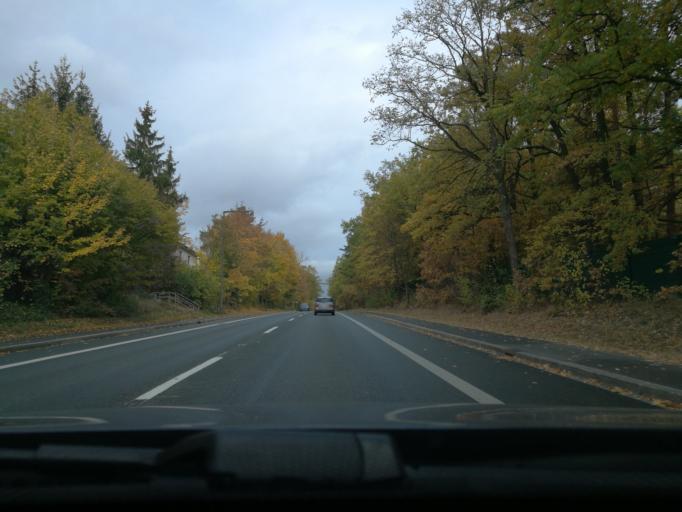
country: DE
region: Bavaria
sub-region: Regierungsbezirk Mittelfranken
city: Furth
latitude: 49.4952
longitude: 10.9875
